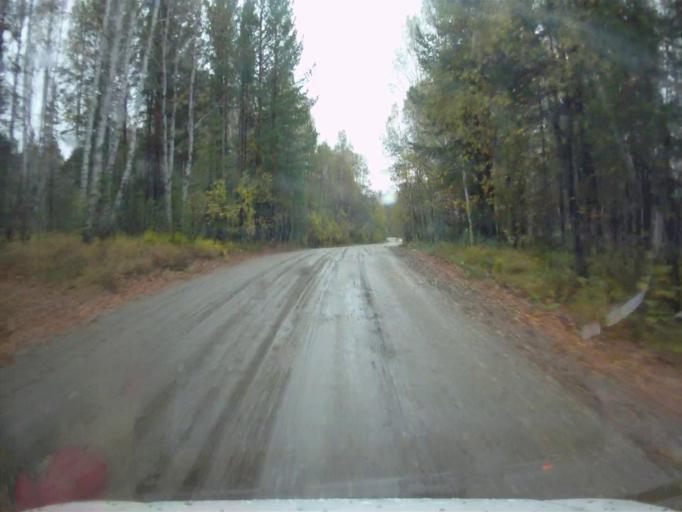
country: RU
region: Chelyabinsk
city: Kyshtym
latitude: 55.8296
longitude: 60.4866
